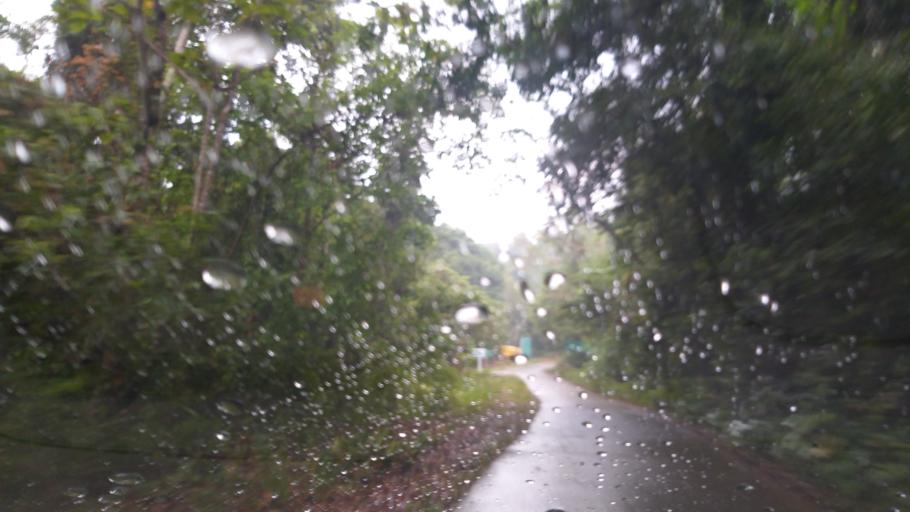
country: TH
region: Trat
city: Ko Chang Tai
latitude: 11.9799
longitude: 102.3232
